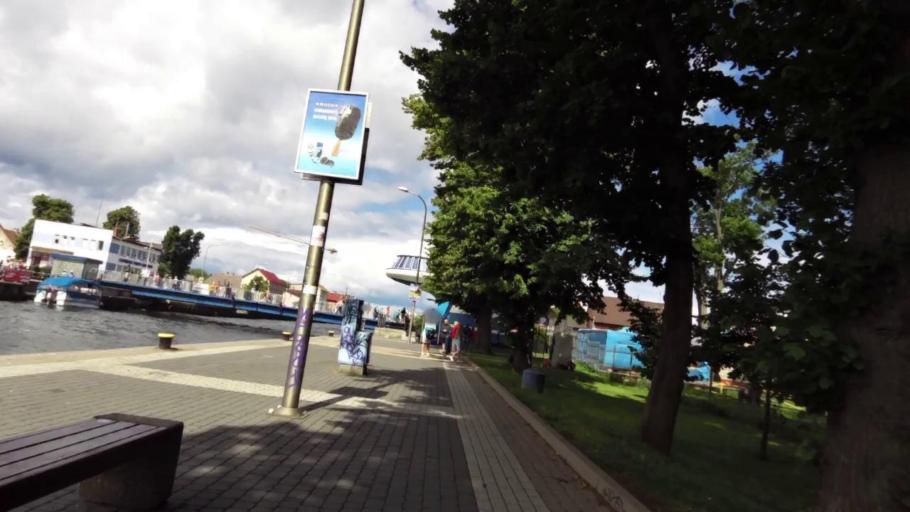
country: PL
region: West Pomeranian Voivodeship
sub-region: Powiat slawienski
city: Darlowo
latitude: 54.4392
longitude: 16.3811
